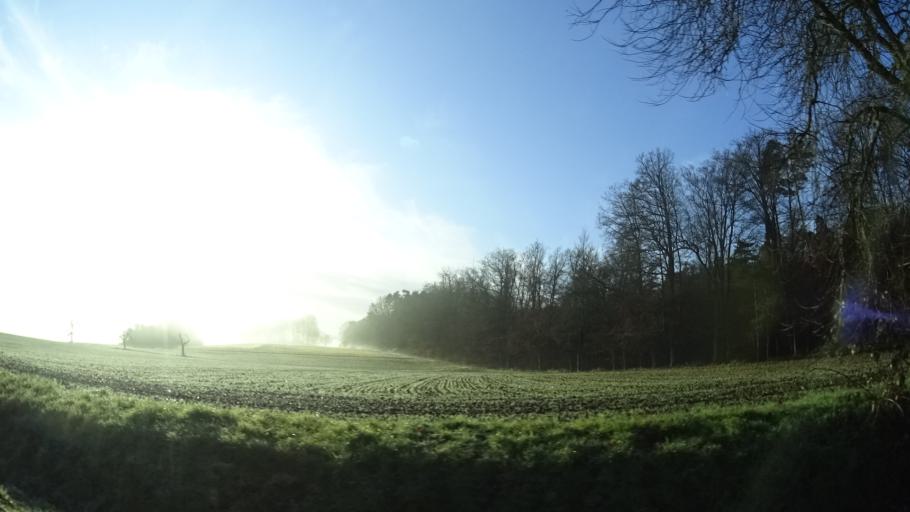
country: DE
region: Bavaria
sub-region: Regierungsbezirk Unterfranken
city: Neunkirchen
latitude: 49.7298
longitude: 9.3995
